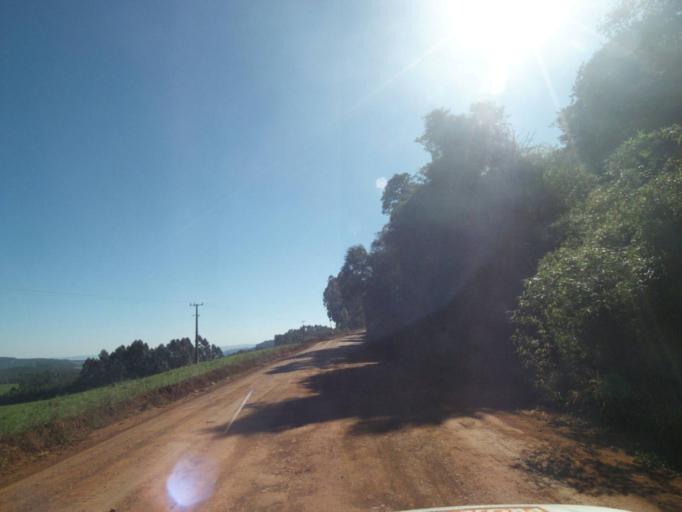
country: BR
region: Parana
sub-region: Tibagi
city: Tibagi
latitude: -24.5941
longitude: -50.6036
